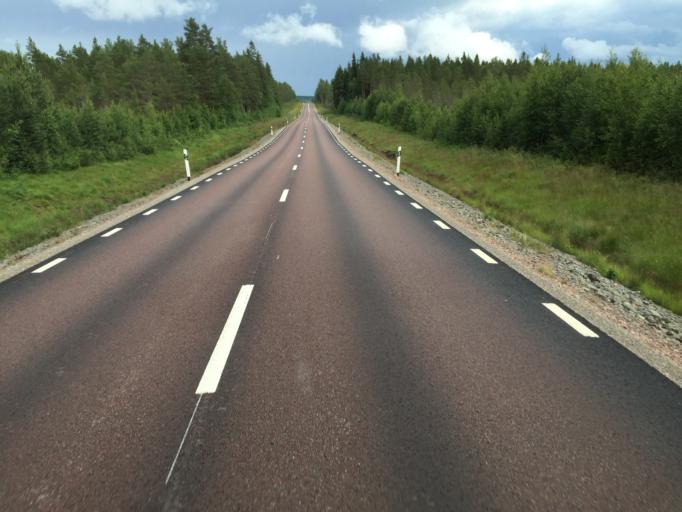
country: SE
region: Dalarna
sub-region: Malung-Saelens kommun
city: Malung
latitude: 60.8246
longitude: 14.0293
